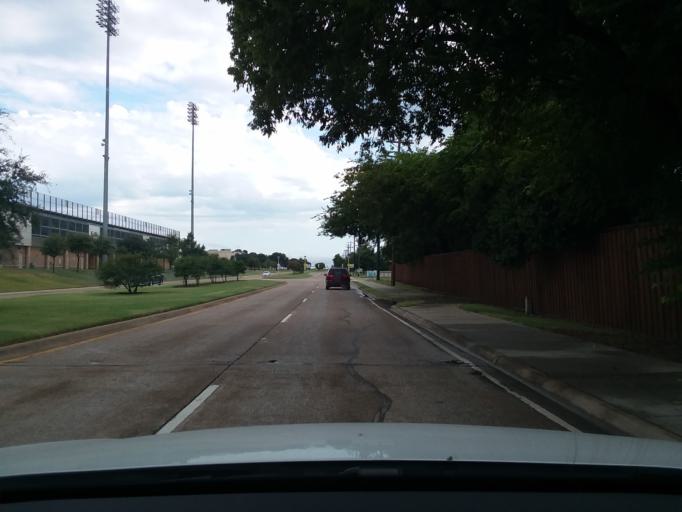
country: US
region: Texas
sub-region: Denton County
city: Highland Village
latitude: 33.0598
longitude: -97.0616
